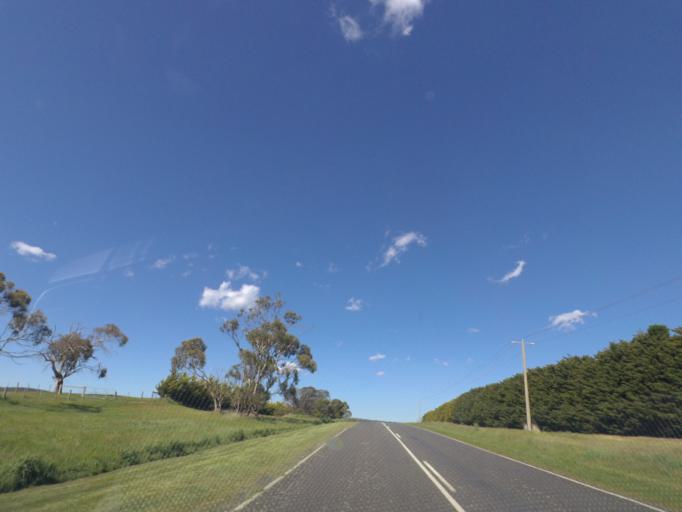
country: AU
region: Victoria
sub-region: Moorabool
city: Bacchus Marsh
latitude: -37.5649
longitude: 144.2819
